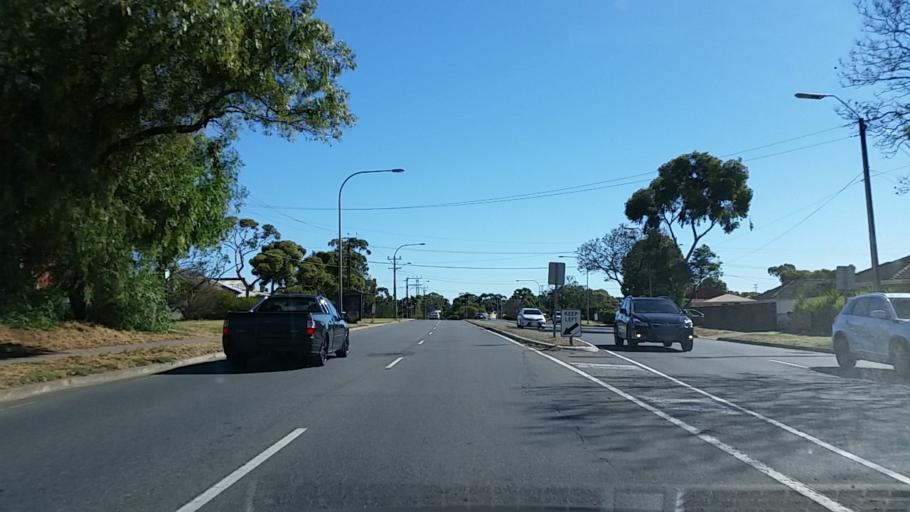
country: AU
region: South Australia
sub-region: Salisbury
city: Ingle Farm
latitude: -34.8335
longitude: 138.6274
